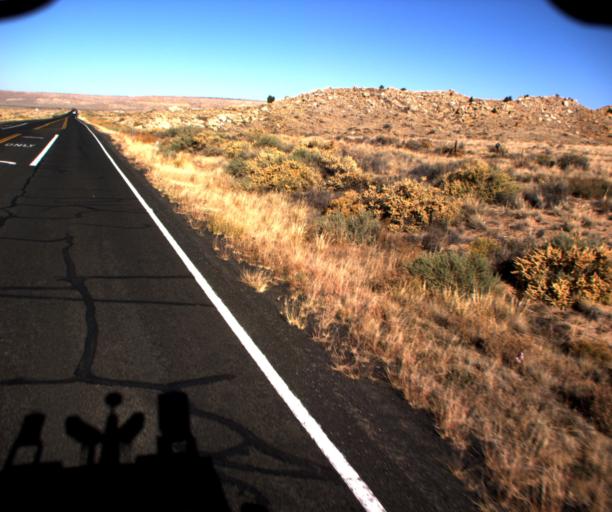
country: US
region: Arizona
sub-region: Navajo County
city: First Mesa
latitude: 35.8328
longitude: -110.2949
